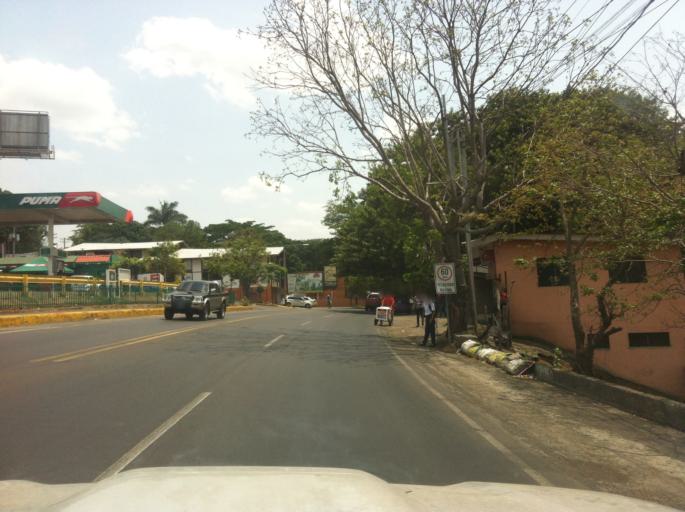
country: NI
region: Managua
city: Ciudad Sandino
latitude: 12.1075
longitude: -86.3174
